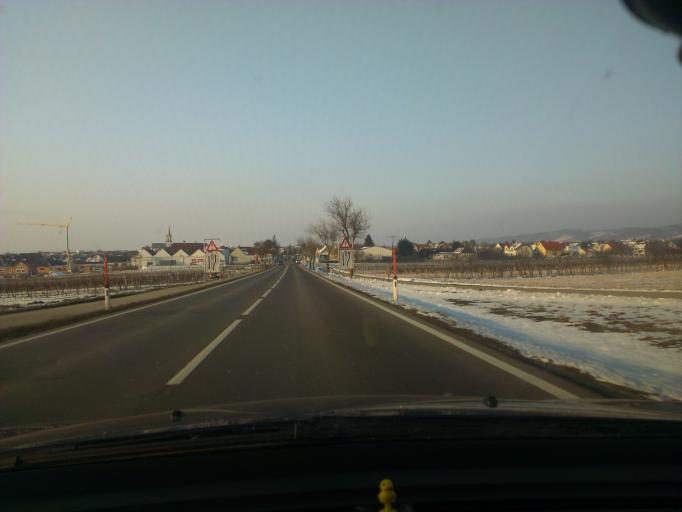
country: AT
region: Burgenland
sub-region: Eisenstadt-Umgebung
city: Breitenbrunn
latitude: 47.9197
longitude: 16.7019
